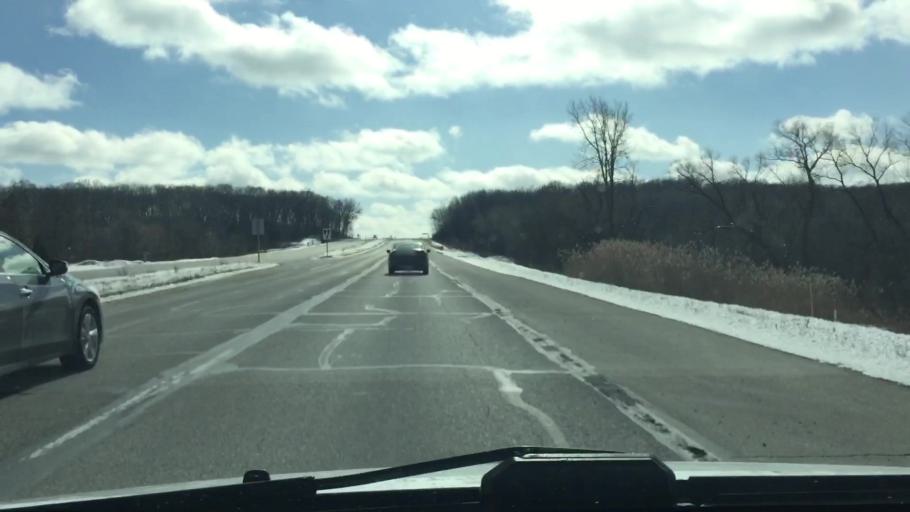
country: US
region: Wisconsin
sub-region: Waukesha County
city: Big Bend
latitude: 42.9418
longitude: -88.2284
